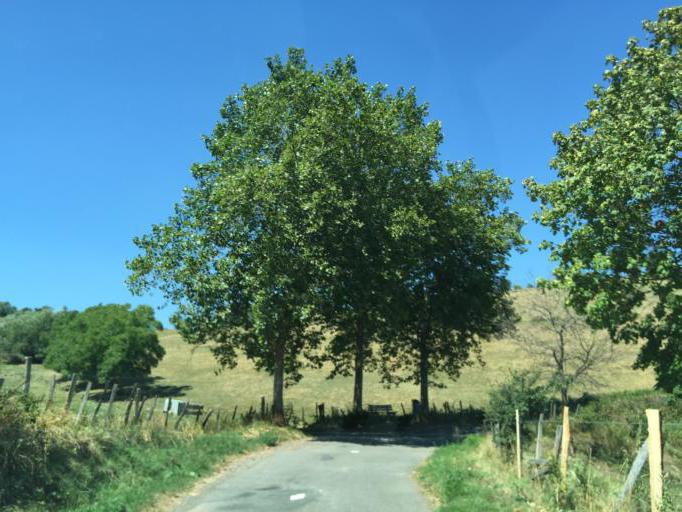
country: FR
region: Rhone-Alpes
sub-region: Departement de la Loire
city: Saint-Jean-Bonnefonds
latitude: 45.4680
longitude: 4.4635
